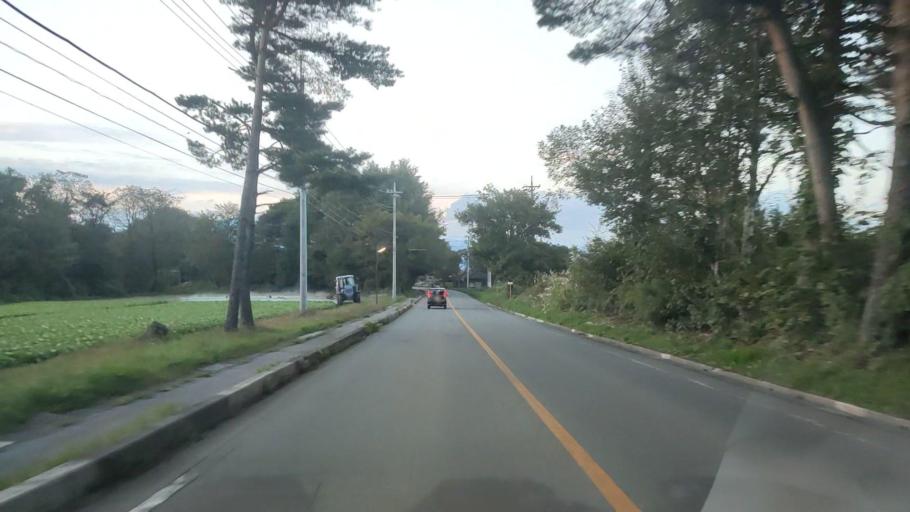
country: JP
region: Nagano
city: Komoro
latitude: 36.4824
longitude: 138.5856
